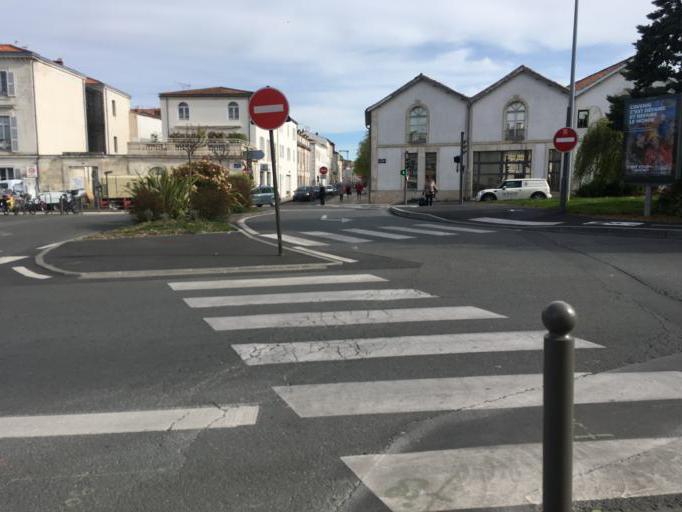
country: FR
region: Poitou-Charentes
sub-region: Departement de la Charente-Maritime
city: La Rochelle
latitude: 46.1586
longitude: -1.1465
